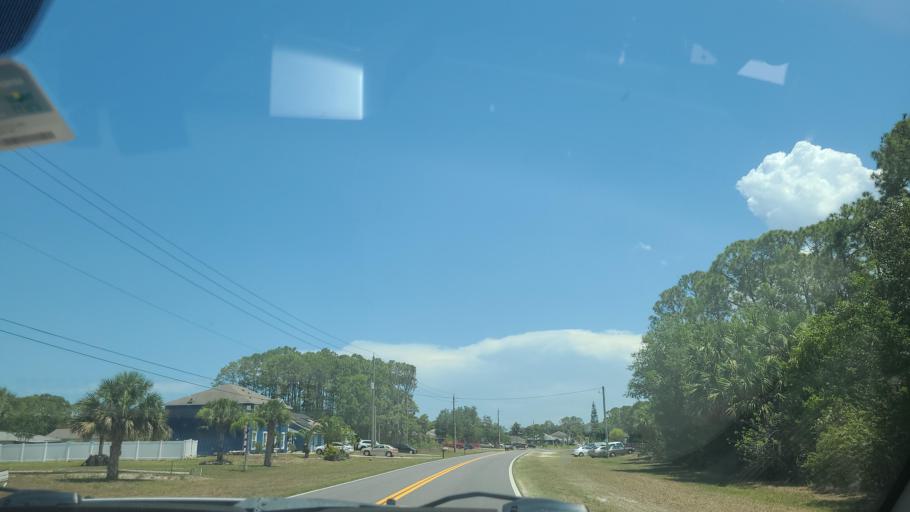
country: US
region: Florida
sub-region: Brevard County
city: Grant-Valkaria
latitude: 27.9309
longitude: -80.6333
